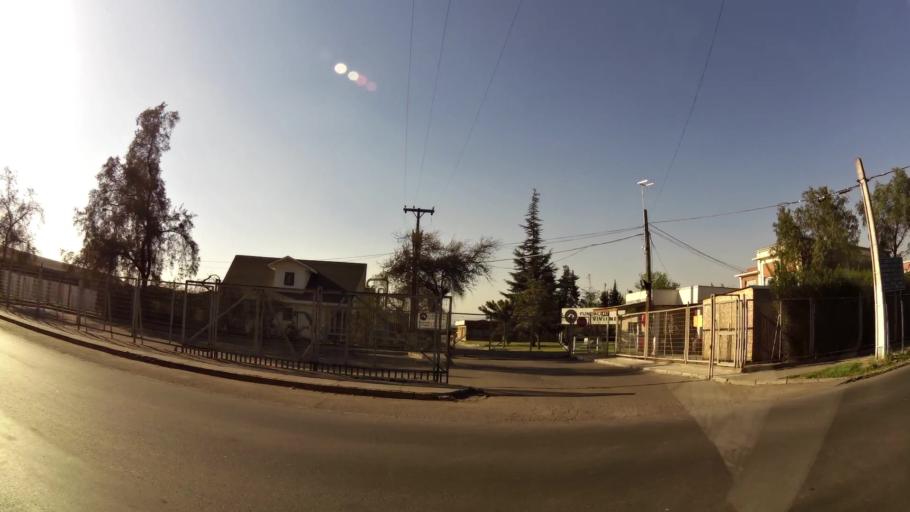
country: CL
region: Santiago Metropolitan
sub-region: Provincia de Santiago
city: La Pintana
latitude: -33.5493
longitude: -70.6282
